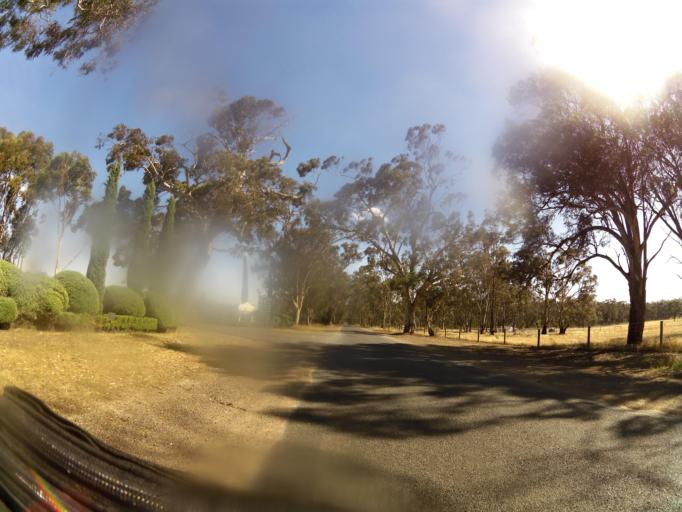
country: AU
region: Victoria
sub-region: Campaspe
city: Kyabram
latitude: -36.8655
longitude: 145.0874
